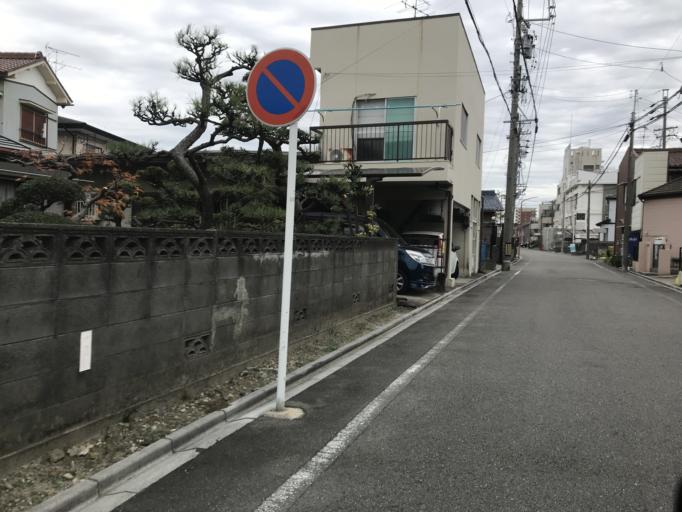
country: JP
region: Aichi
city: Nagoya-shi
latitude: 35.1949
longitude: 136.8532
